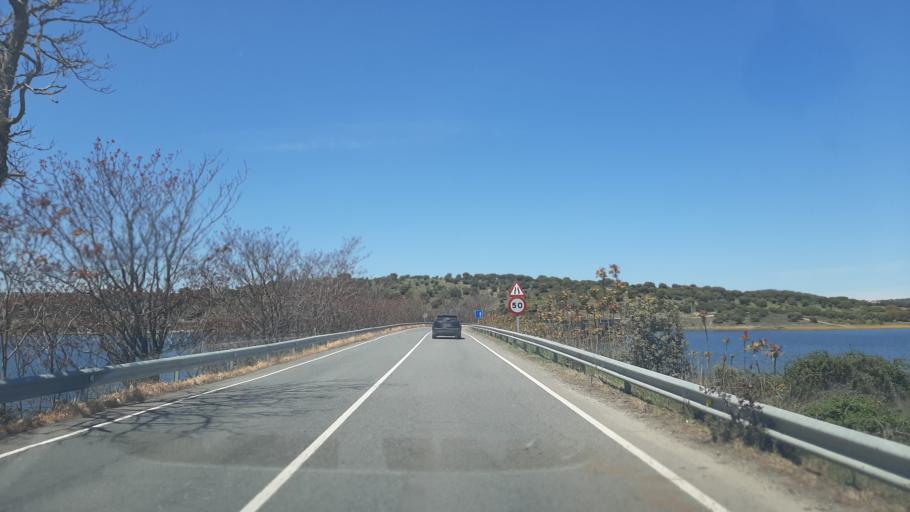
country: ES
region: Castille and Leon
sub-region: Provincia de Salamanca
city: Guijo de Avila
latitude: 40.5509
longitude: -5.6266
